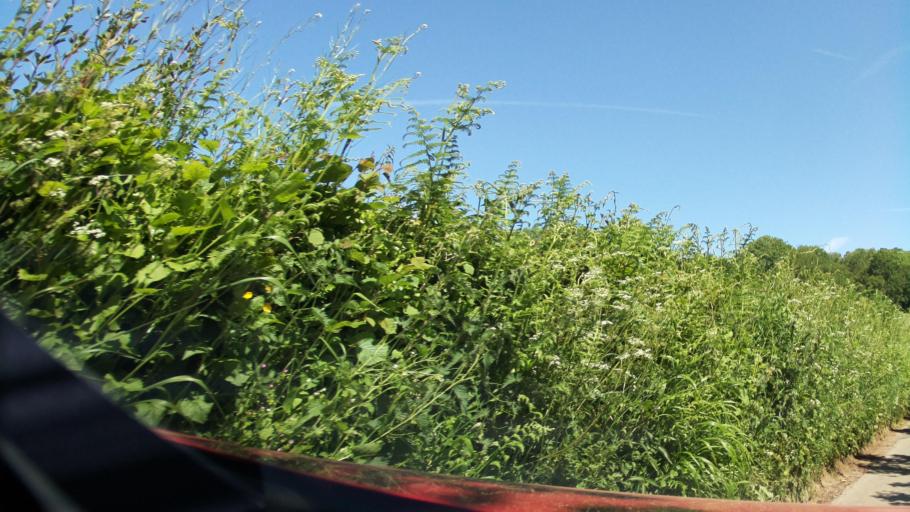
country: GB
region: Wales
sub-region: Monmouthshire
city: Magor
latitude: 51.5933
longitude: -2.8181
